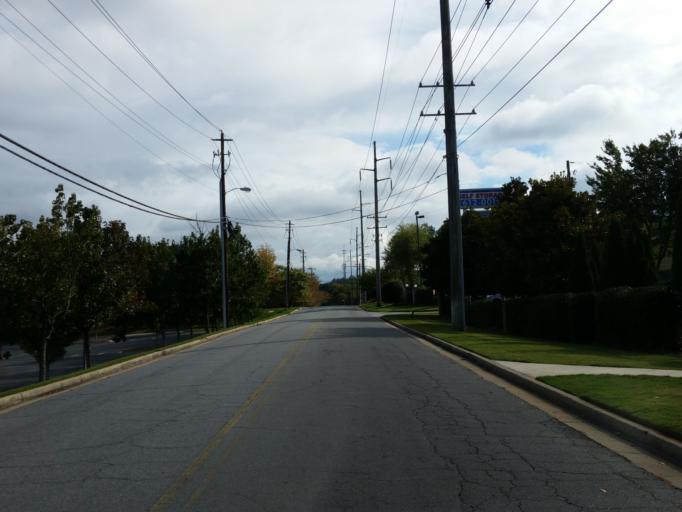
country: US
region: Georgia
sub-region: Cobb County
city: Smyrna
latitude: 33.9254
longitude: -84.4823
